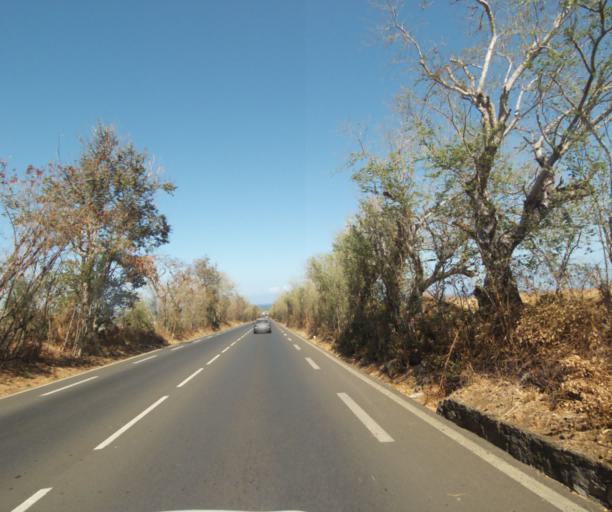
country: RE
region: Reunion
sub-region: Reunion
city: Le Port
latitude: -20.9817
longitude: 55.3101
